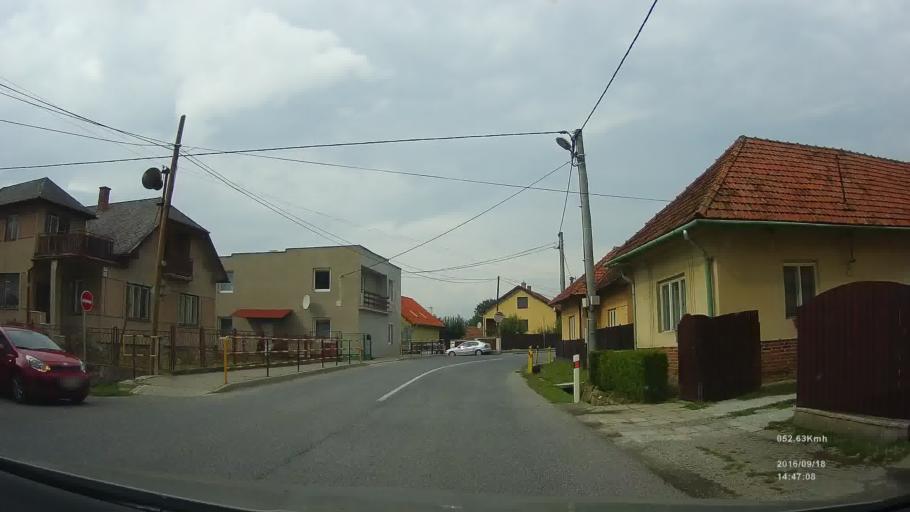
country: SK
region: Kosicky
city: Spisska Nova Ves
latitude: 48.9638
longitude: 20.5823
